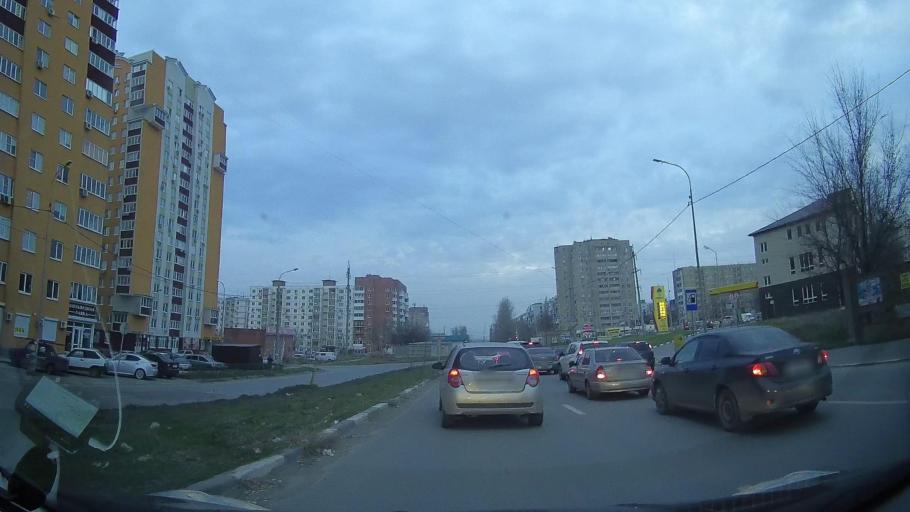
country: RU
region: Rostov
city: Severnyy
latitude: 47.3033
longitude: 39.7226
